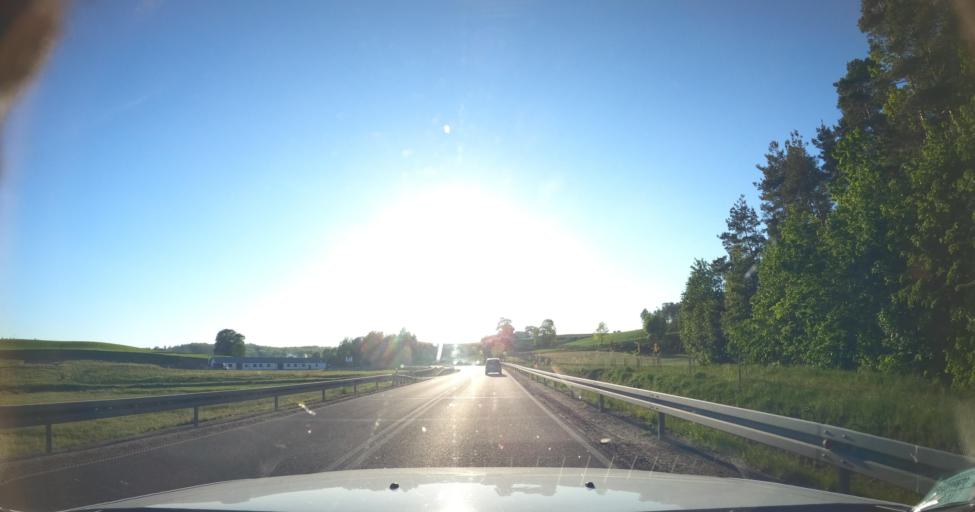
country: PL
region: Pomeranian Voivodeship
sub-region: Powiat kartuski
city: Chmielno
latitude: 54.3431
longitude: 18.0086
